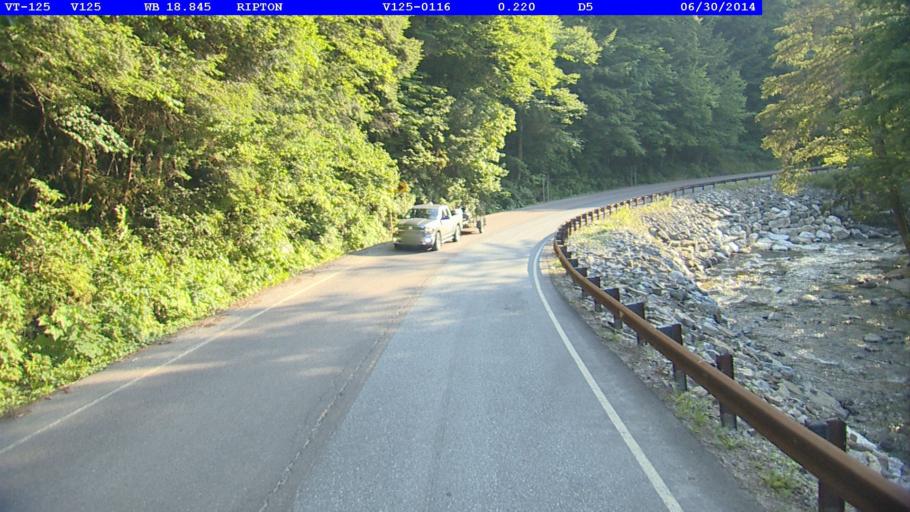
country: US
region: Vermont
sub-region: Addison County
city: Middlebury (village)
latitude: 43.9716
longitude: -73.0551
